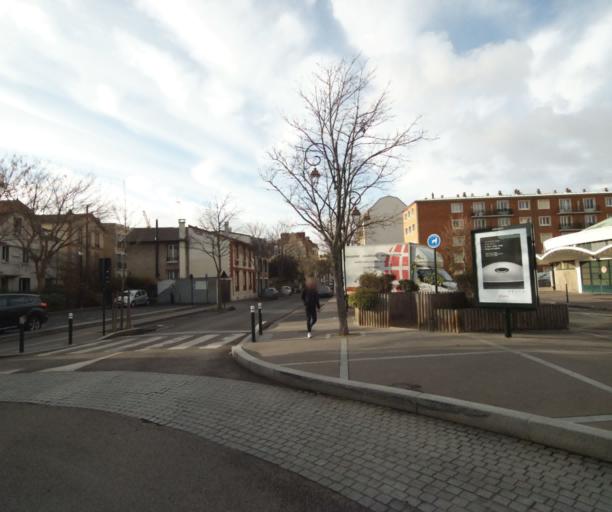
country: FR
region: Ile-de-France
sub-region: Departement des Hauts-de-Seine
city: Colombes
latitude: 48.9110
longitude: 2.2570
